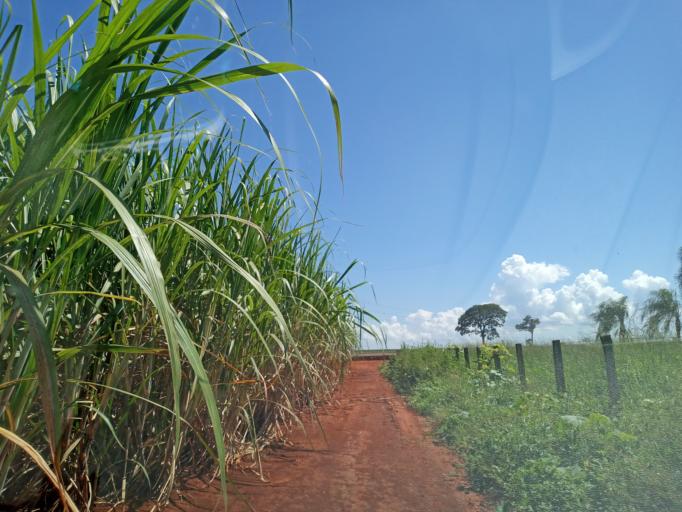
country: BR
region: Goias
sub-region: Itumbiara
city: Itumbiara
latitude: -18.4412
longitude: -49.1345
